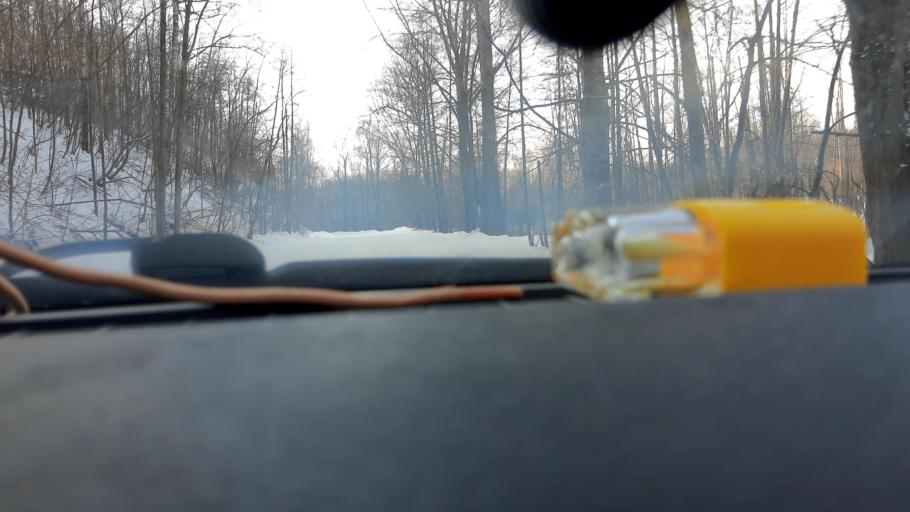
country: RU
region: Bashkortostan
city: Kabakovo
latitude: 54.6278
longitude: 56.0518
